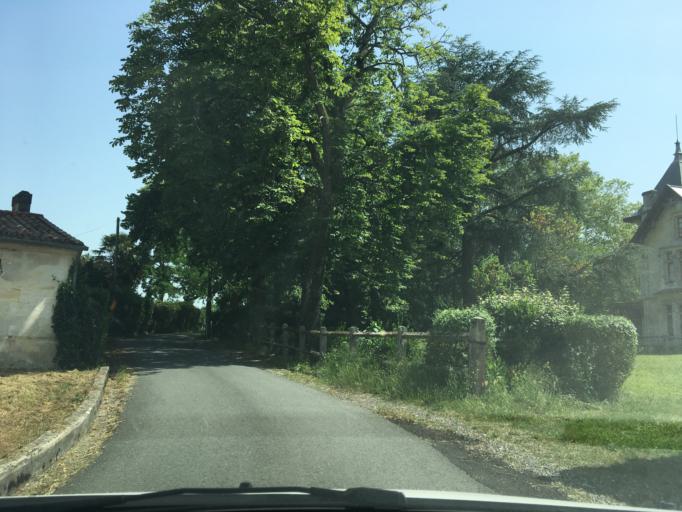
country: FR
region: Aquitaine
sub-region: Departement de la Gironde
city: Cantenac
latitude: 45.0143
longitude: -0.6410
